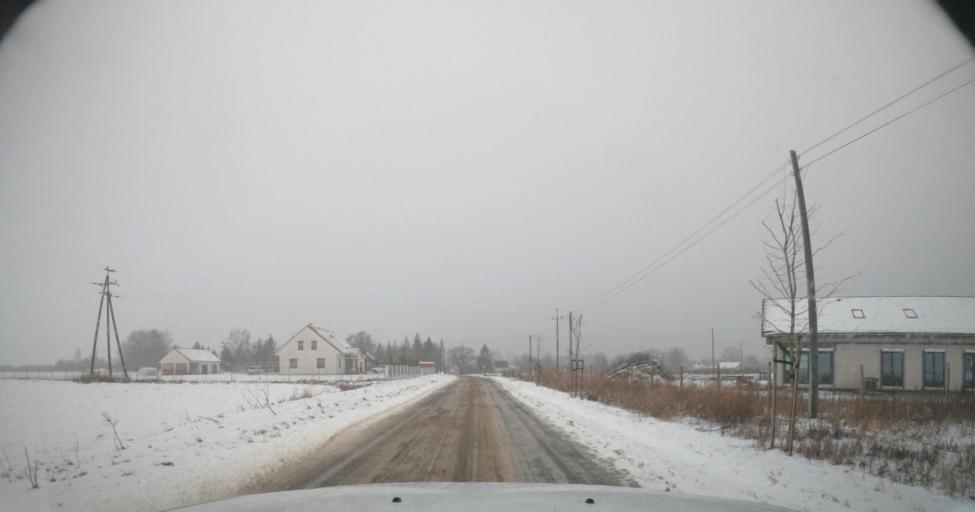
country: PL
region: West Pomeranian Voivodeship
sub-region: Powiat kamienski
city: Golczewo
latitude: 53.8082
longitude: 14.9657
